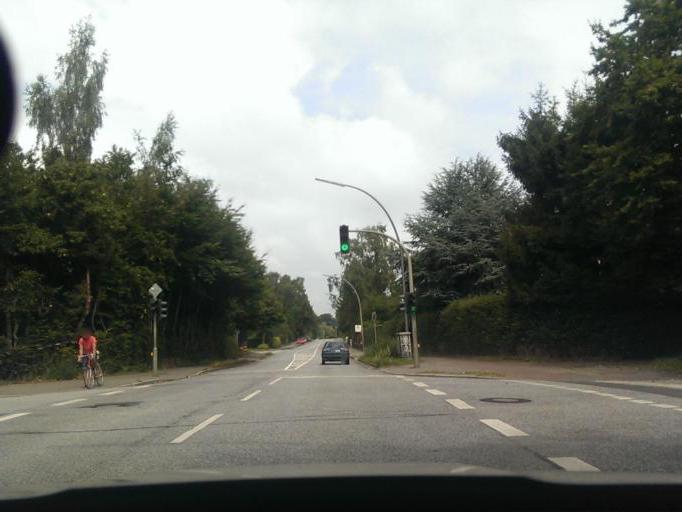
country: DE
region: Hamburg
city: Poppenbuettel
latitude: 53.6553
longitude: 10.0770
